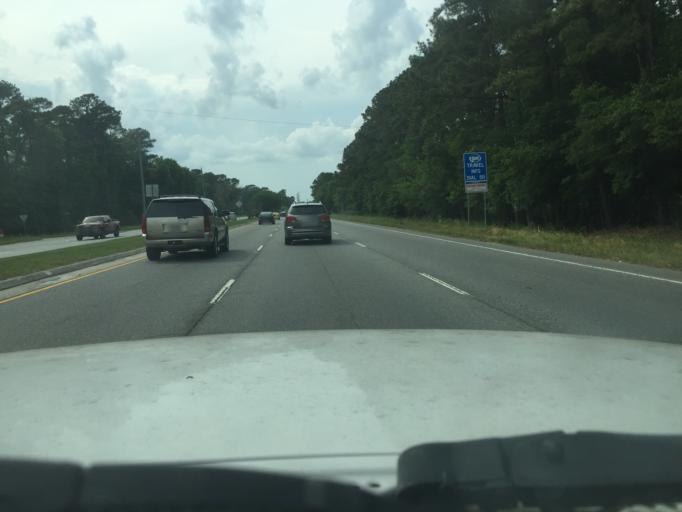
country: US
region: Georgia
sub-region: Chatham County
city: Whitemarsh Island
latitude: 32.0380
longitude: -80.9920
